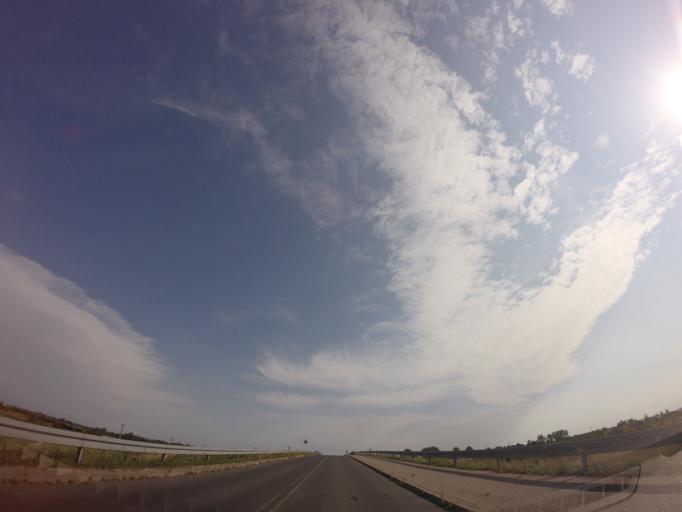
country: PL
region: West Pomeranian Voivodeship
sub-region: Powiat stargardzki
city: Stargard Szczecinski
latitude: 53.3073
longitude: 15.0468
